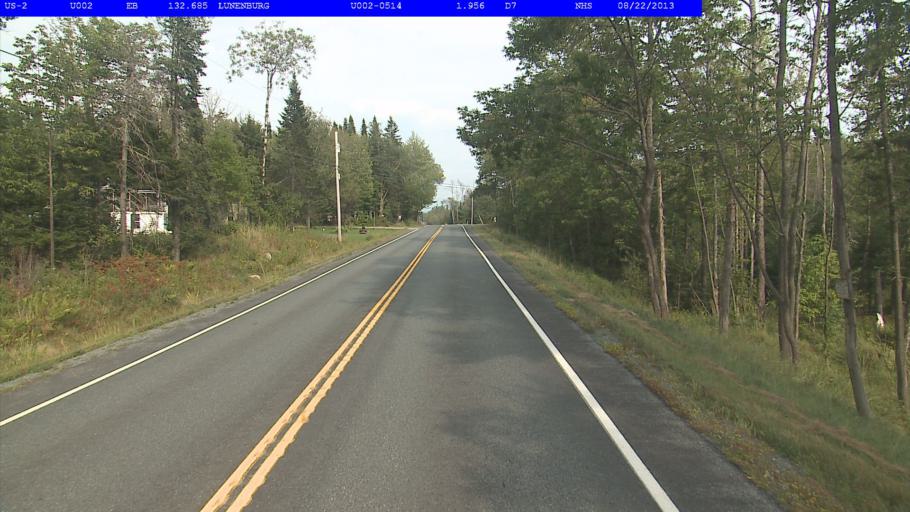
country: US
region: New Hampshire
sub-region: Coos County
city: Whitefield
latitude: 44.4644
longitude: -71.7367
